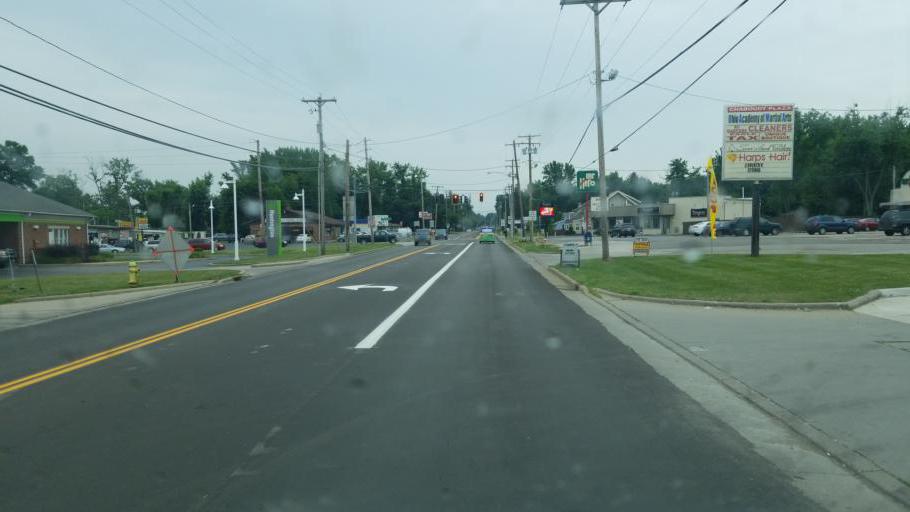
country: US
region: Ohio
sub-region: Summit County
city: Portage Lakes
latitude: 41.0066
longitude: -81.5557
